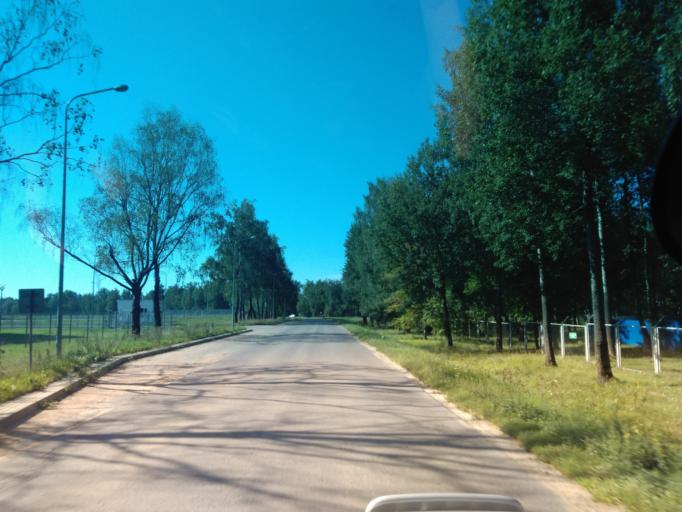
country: BY
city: Fanipol
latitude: 53.7259
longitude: 27.3388
